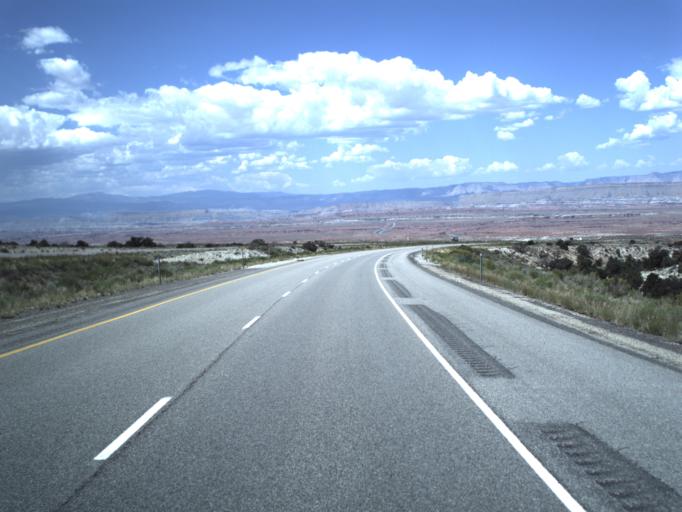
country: US
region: Utah
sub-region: Emery County
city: Ferron
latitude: 38.8417
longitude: -110.9583
